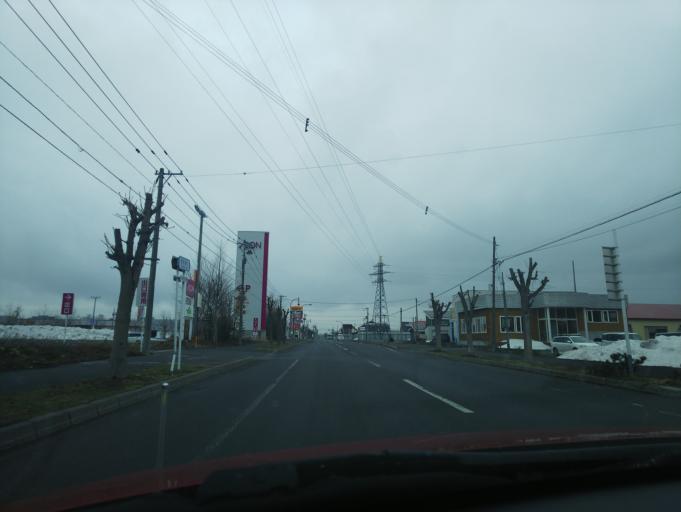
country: JP
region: Hokkaido
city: Nayoro
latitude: 44.3388
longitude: 142.4503
